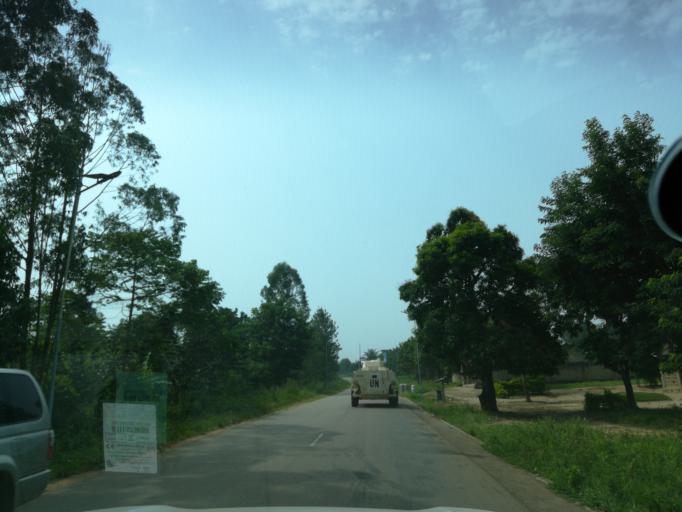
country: CD
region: Nord Kivu
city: Beni
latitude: 0.5673
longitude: 29.4775
